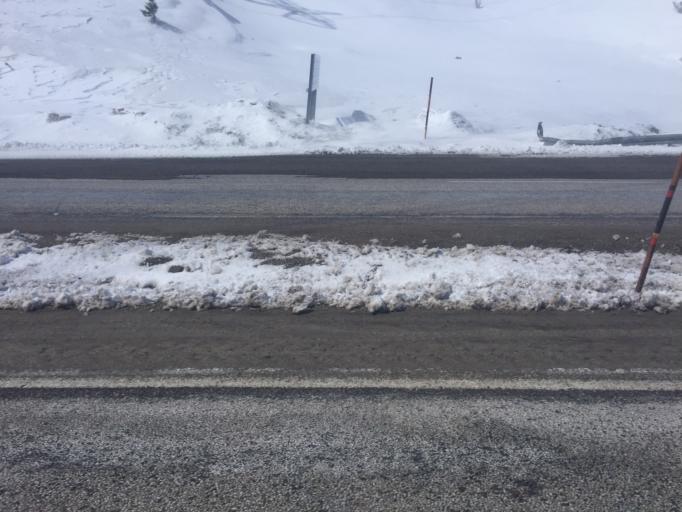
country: TR
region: Kahramanmaras
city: Goksun
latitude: 38.1926
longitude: 36.4569
